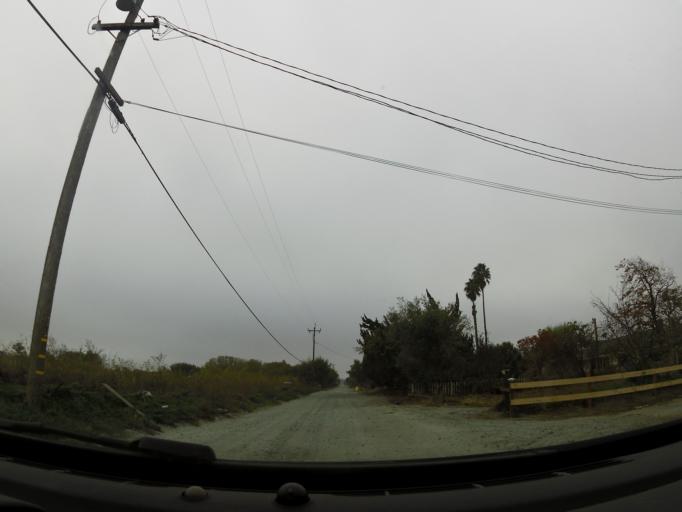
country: US
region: California
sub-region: San Benito County
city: Hollister
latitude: 36.9578
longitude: -121.4300
